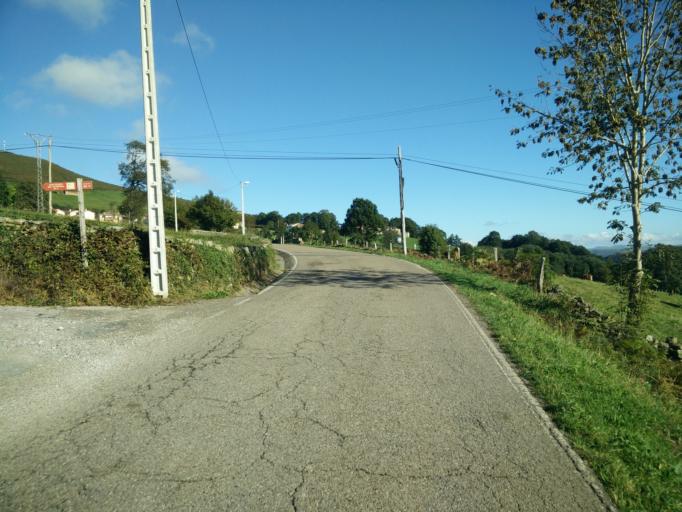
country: ES
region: Cantabria
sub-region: Provincia de Cantabria
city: San Pedro del Romeral
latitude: 43.1140
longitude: -3.8137
